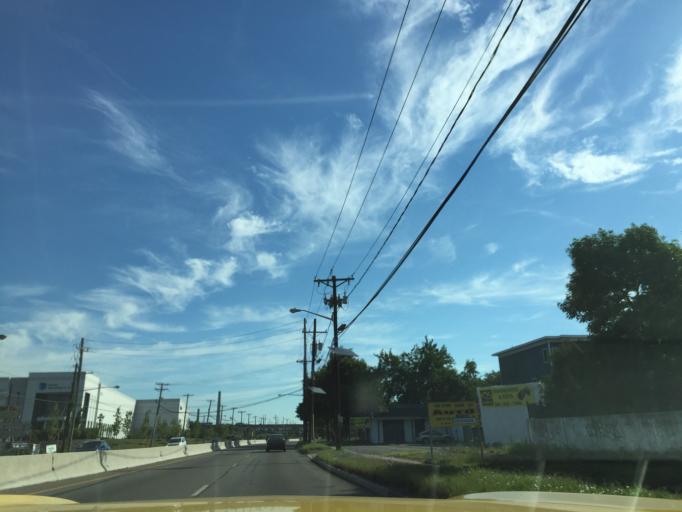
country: US
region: New Jersey
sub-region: Hudson County
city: Jersey City
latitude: 40.7311
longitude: -74.0847
